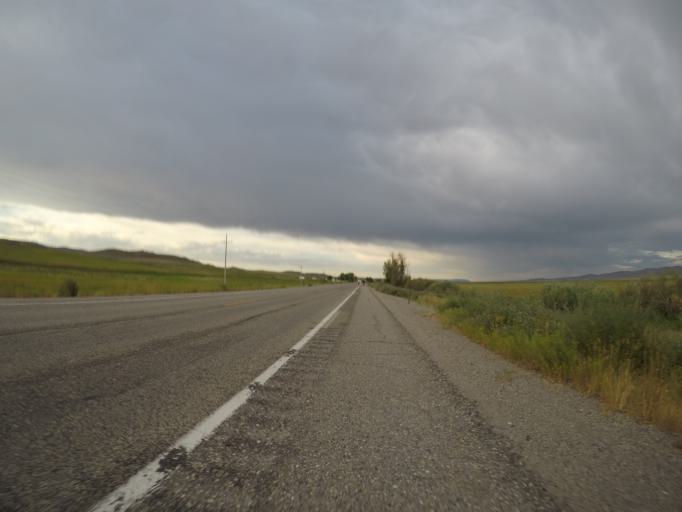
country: US
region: Utah
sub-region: Rich County
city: Randolph
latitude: 42.0318
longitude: -110.9326
